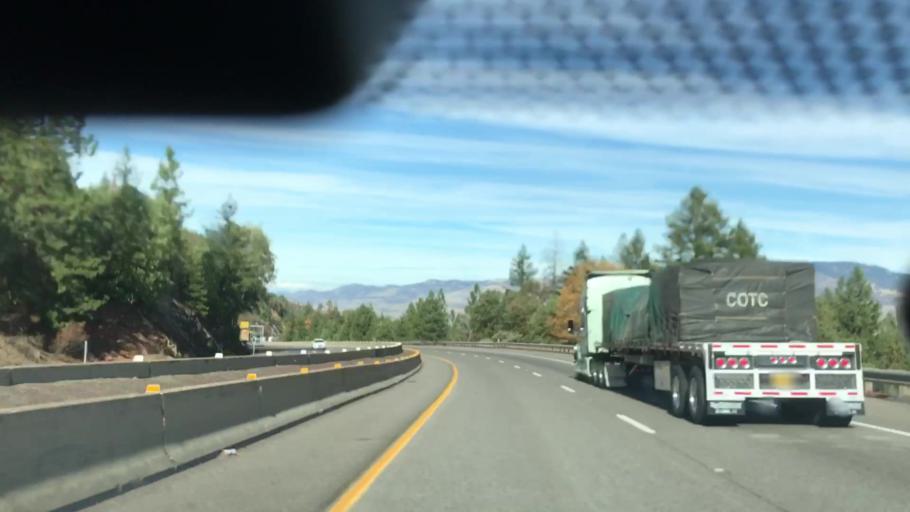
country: US
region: Oregon
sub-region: Jackson County
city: Ashland
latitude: 42.1209
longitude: -122.6236
